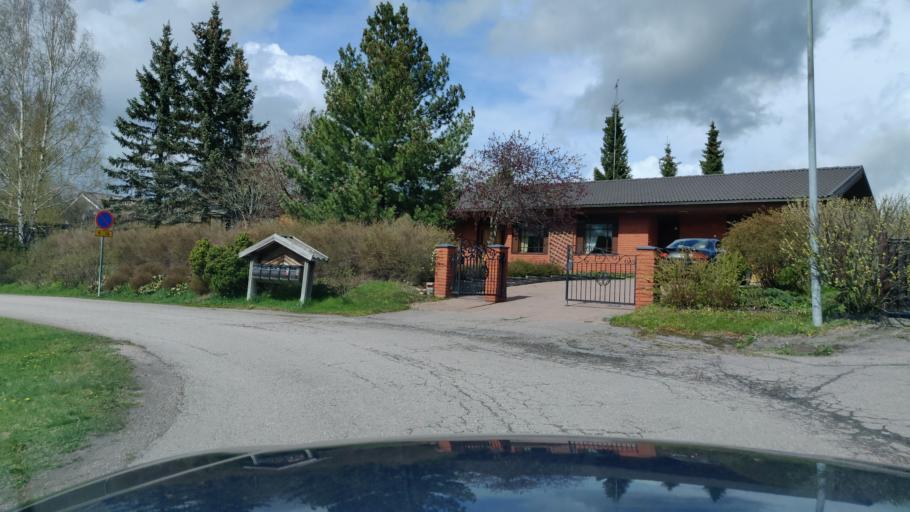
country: FI
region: Uusimaa
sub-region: Helsinki
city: Nurmijaervi
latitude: 60.3644
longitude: 24.7404
